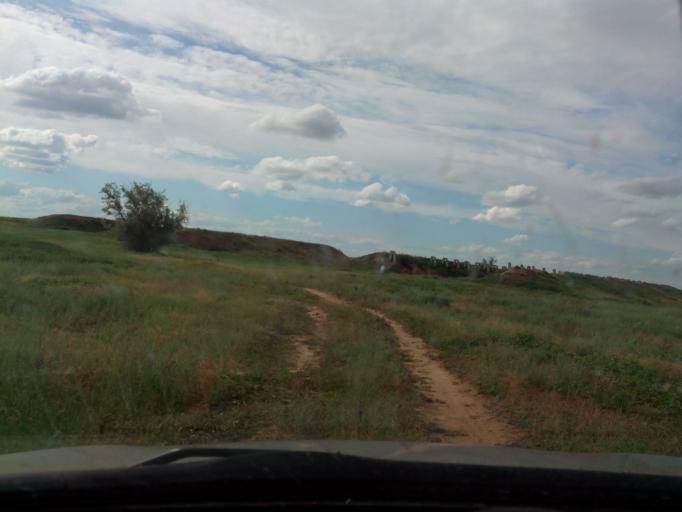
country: RU
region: Volgograd
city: Leninsk
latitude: 48.6805
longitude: 45.3697
